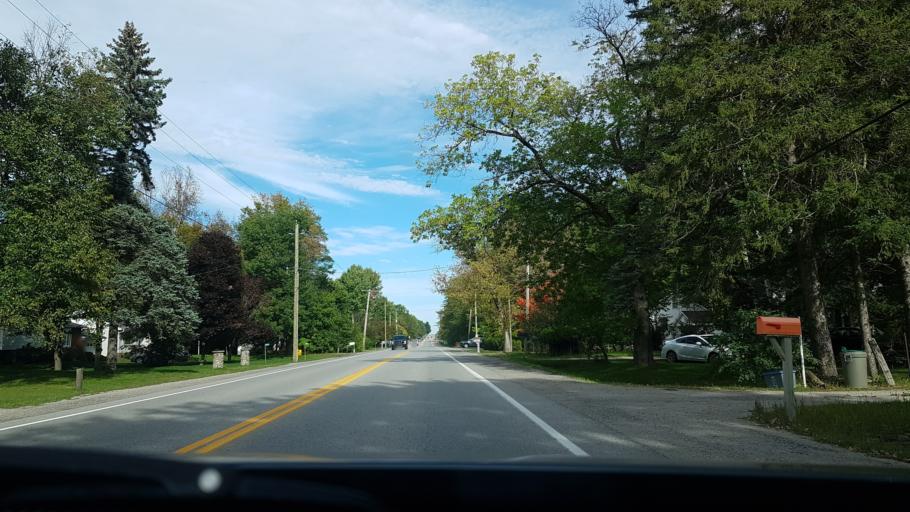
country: CA
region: Ontario
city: Barrie
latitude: 44.4867
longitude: -79.8200
